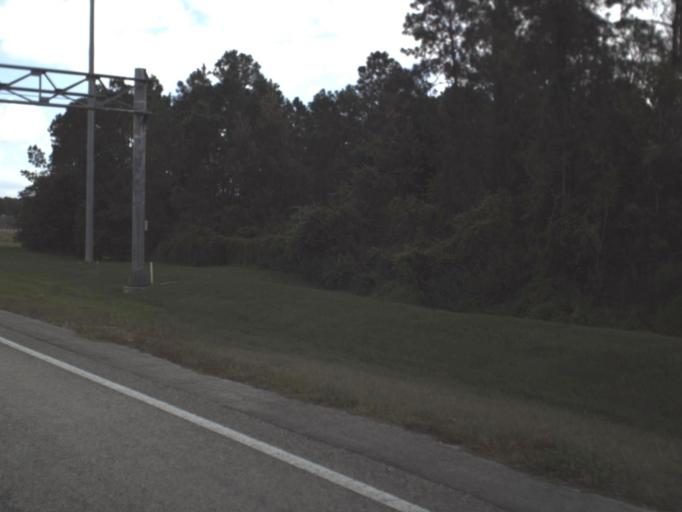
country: US
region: Florida
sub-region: Osceola County
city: Celebration
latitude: 28.3454
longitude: -81.5400
